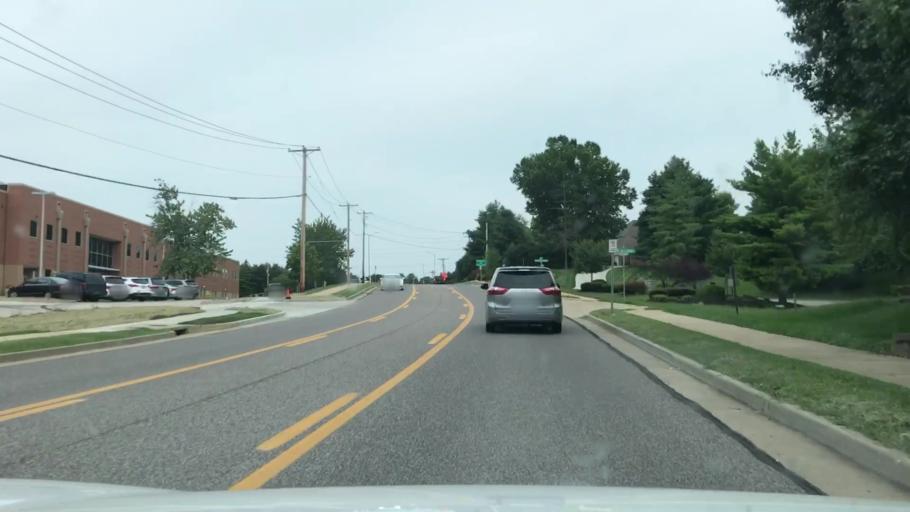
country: US
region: Missouri
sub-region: Saint Louis County
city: Clarkson Valley
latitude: 38.6230
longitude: -90.5846
